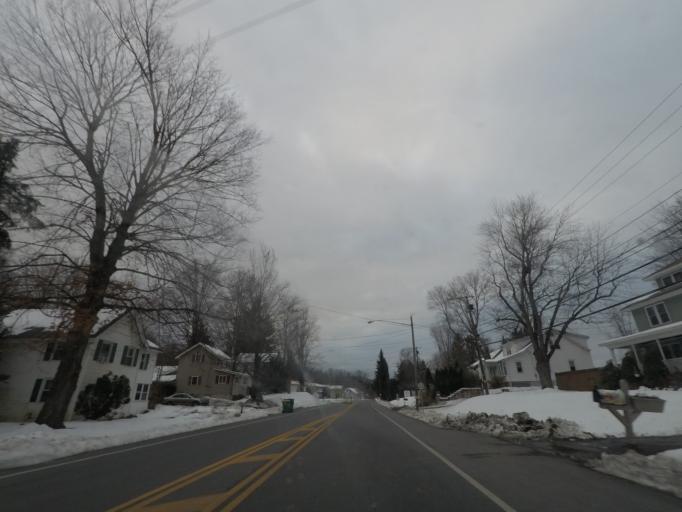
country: US
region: New York
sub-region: Ulster County
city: Plattekill
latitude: 41.6654
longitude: -74.1073
